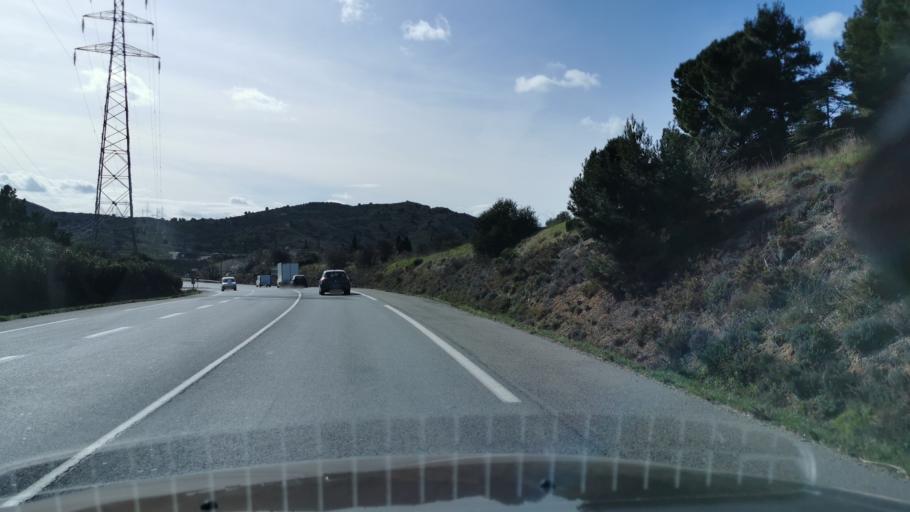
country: FR
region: Languedoc-Roussillon
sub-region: Departement de l'Aude
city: Narbonne
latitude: 43.1838
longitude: 2.9689
